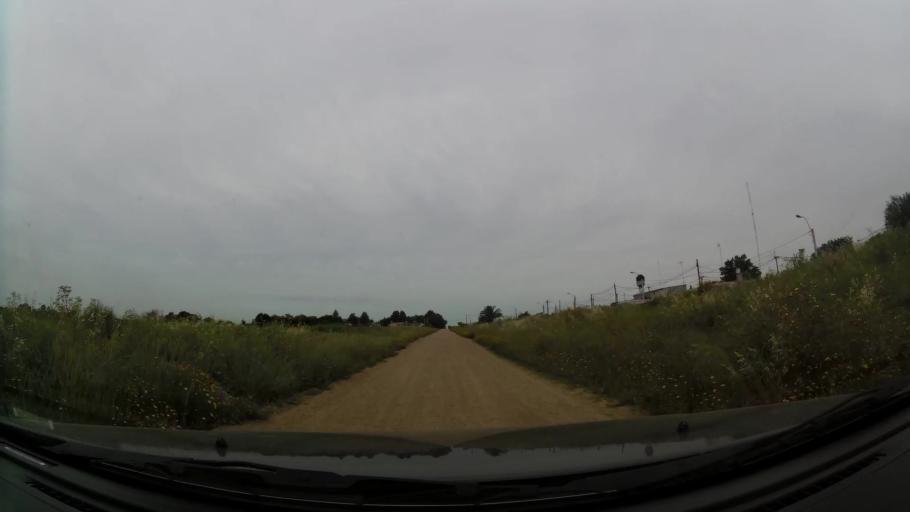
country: UY
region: Canelones
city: La Paz
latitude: -34.7451
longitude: -56.2214
